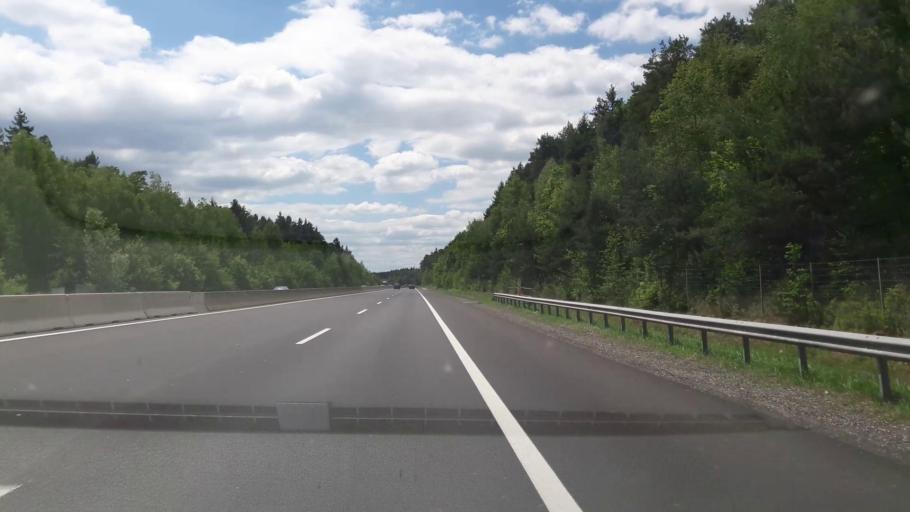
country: AT
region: Styria
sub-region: Politischer Bezirk Hartberg-Fuerstenfeld
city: Bad Waltersdorf
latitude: 47.1483
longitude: 15.9957
